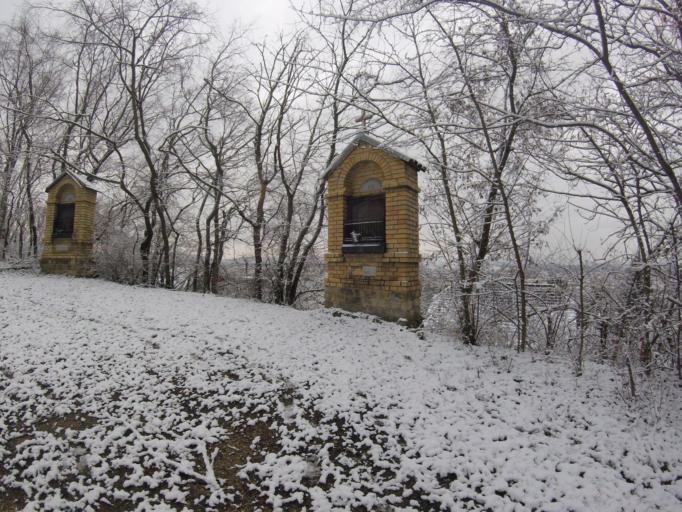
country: HU
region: Komarom-Esztergom
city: Esztergom
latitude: 47.7868
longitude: 18.7505
